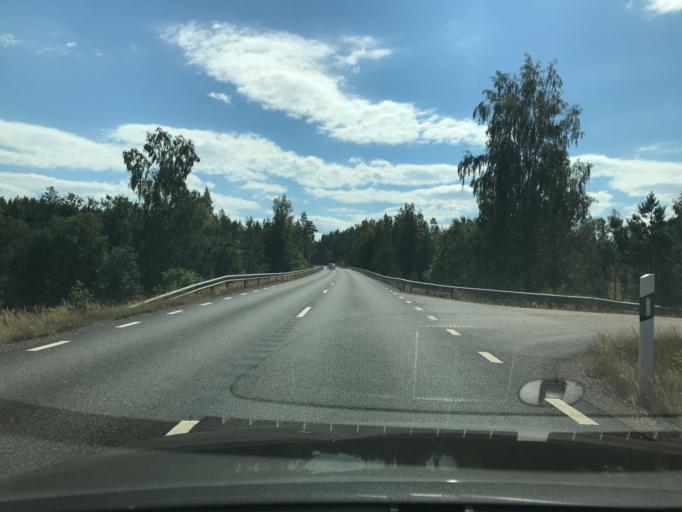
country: SE
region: Kalmar
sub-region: Hultsfreds Kommun
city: Virserum
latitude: 57.2850
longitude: 15.5662
